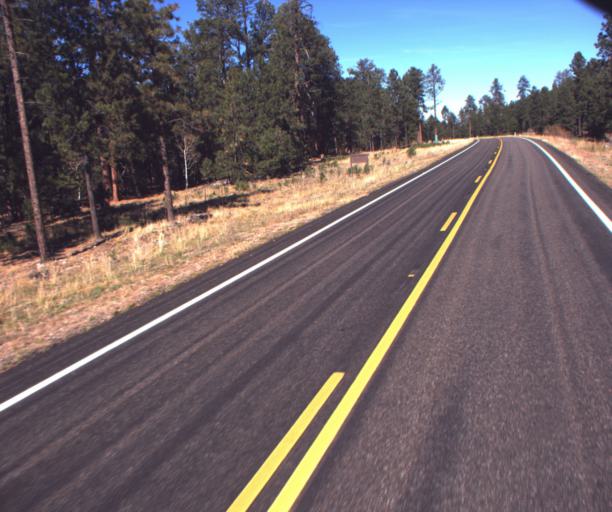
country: US
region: Arizona
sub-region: Coconino County
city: Fredonia
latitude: 36.6909
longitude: -112.2159
